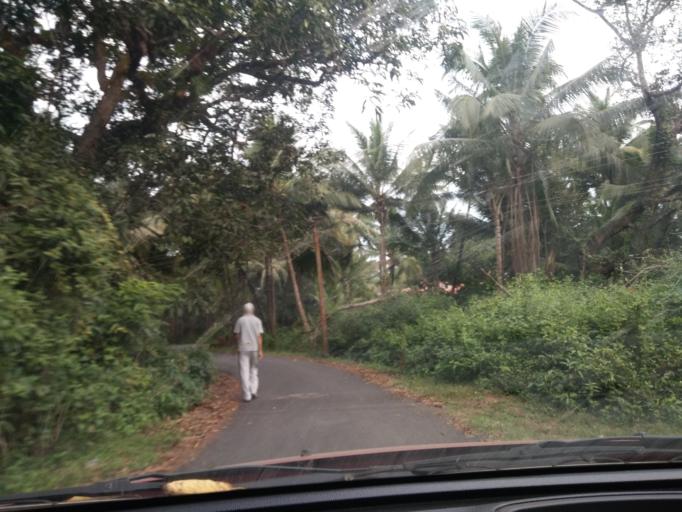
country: IN
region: Goa
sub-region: South Goa
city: Varca
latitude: 15.2222
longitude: 73.9548
